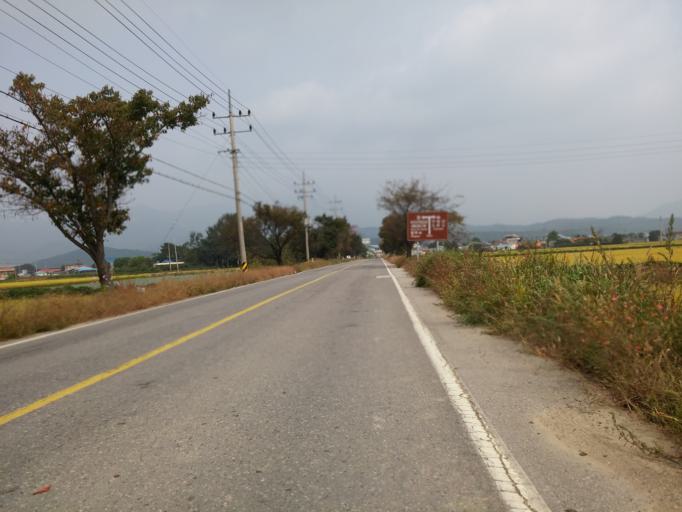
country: KR
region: Chungcheongbuk-do
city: Yong-dong
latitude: 36.4325
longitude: 127.8023
